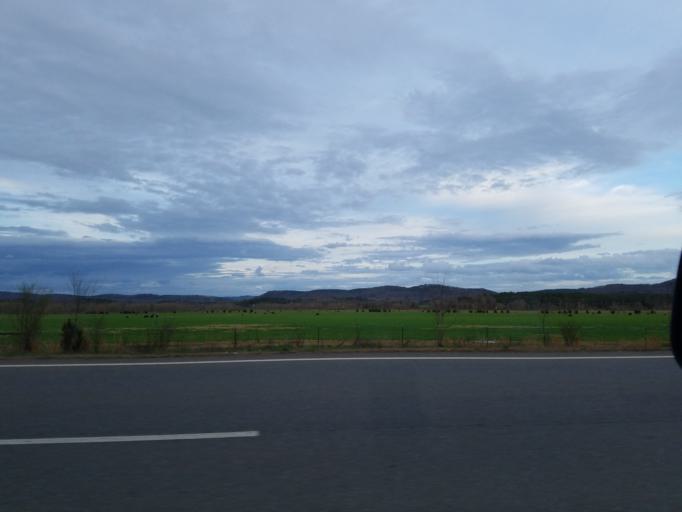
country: US
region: Georgia
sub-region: Bartow County
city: Rydal
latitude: 34.4458
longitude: -84.7251
